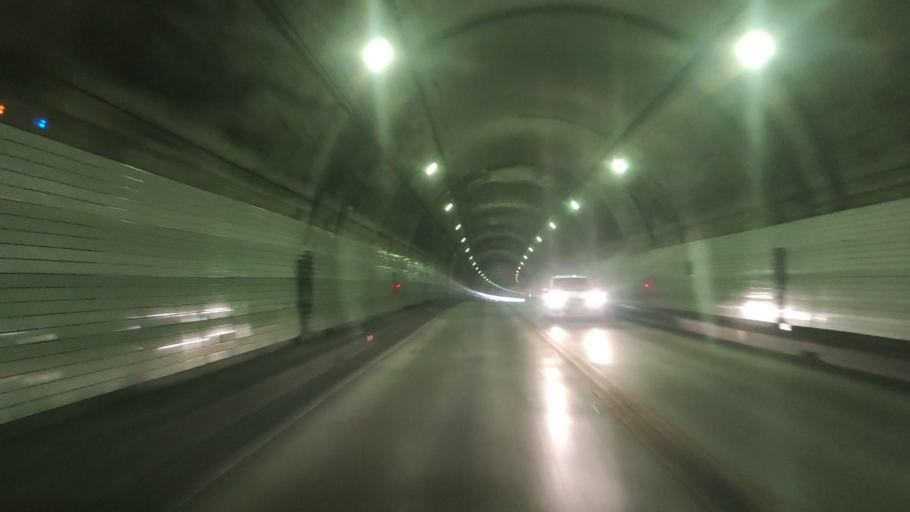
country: JP
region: Fukuoka
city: Maebaru-chuo
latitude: 33.4688
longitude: 130.2811
